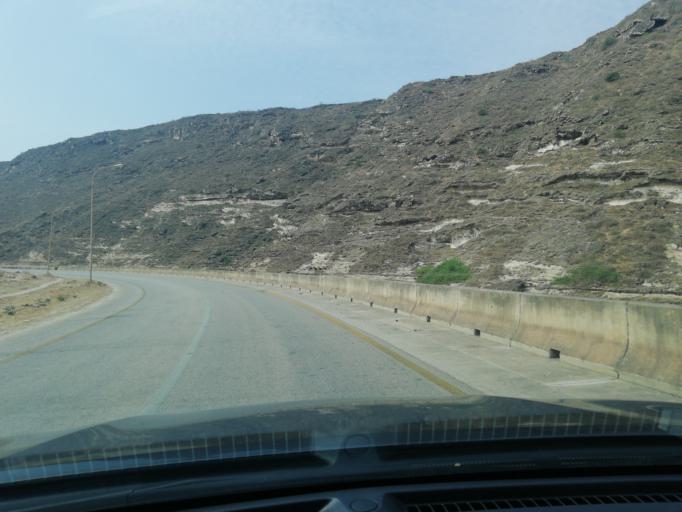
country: OM
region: Zufar
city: Salalah
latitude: 16.8973
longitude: 53.8146
